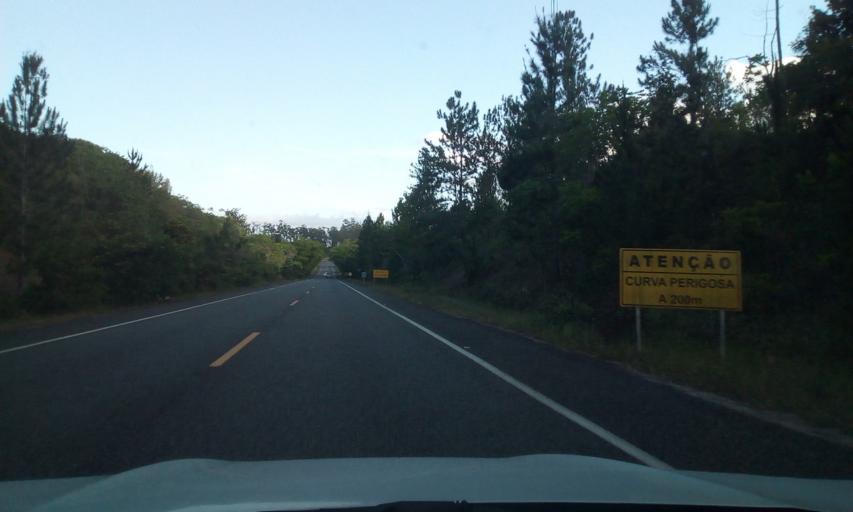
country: BR
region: Bahia
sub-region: Entre Rios
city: Entre Rios
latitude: -12.3137
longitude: -37.9044
